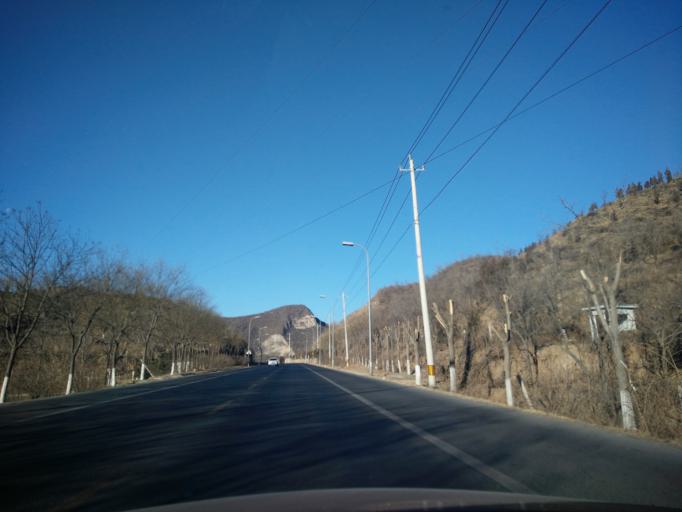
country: CN
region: Beijing
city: Junzhuang
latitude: 39.9911
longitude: 116.0740
